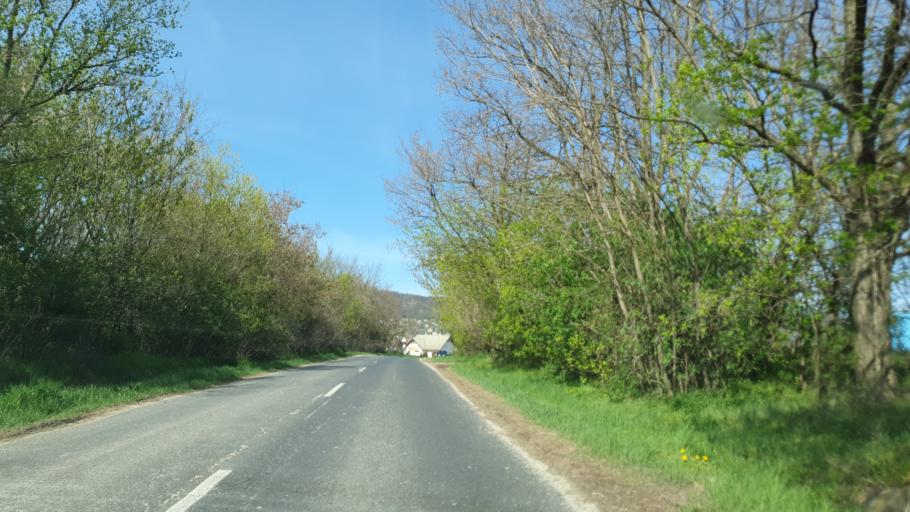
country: HU
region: Fejer
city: Bodajk
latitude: 47.3432
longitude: 18.2606
